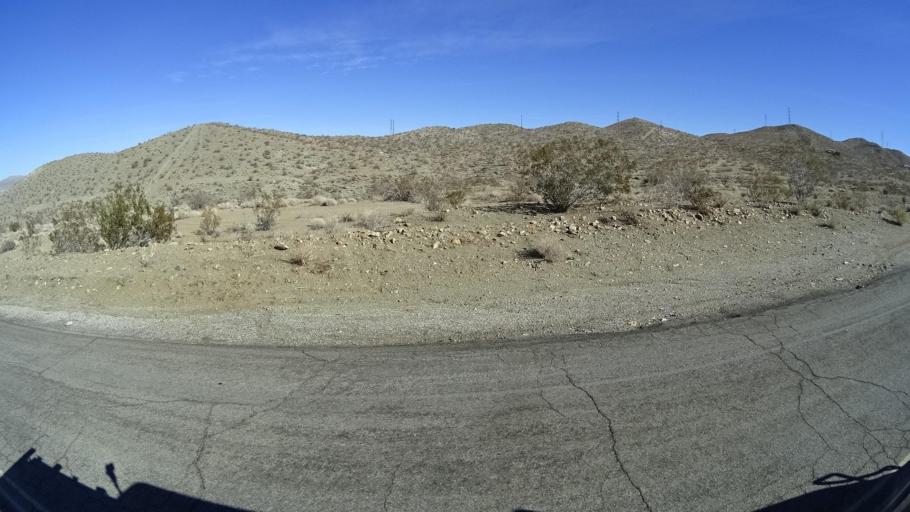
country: US
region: California
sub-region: Kern County
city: Ridgecrest
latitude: 35.3734
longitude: -117.6616
